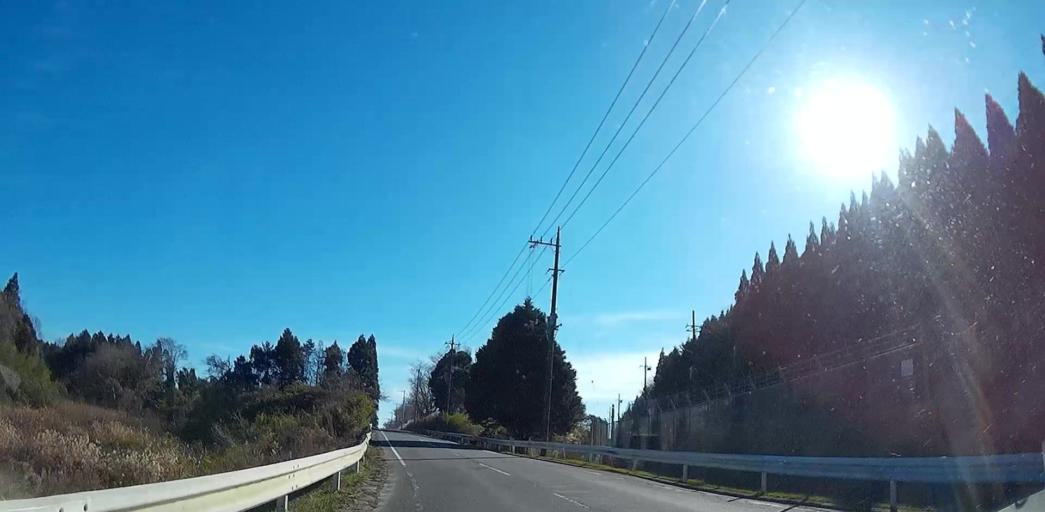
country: JP
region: Chiba
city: Narita
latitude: 35.7951
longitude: 140.3909
